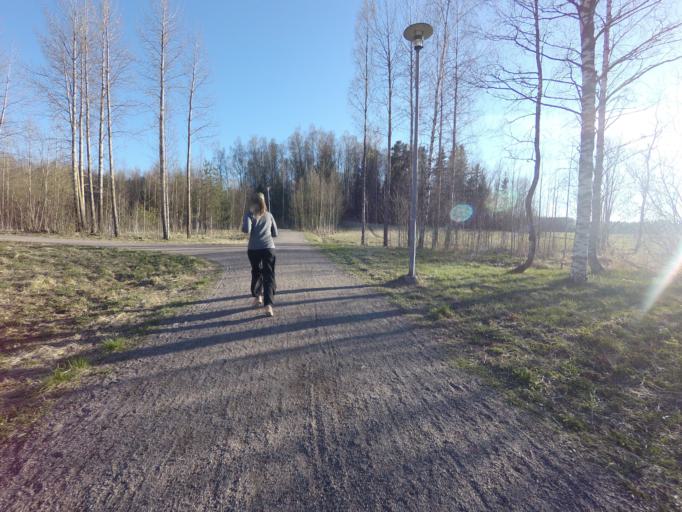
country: FI
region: Uusimaa
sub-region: Helsinki
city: Espoo
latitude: 60.1722
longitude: 24.6740
